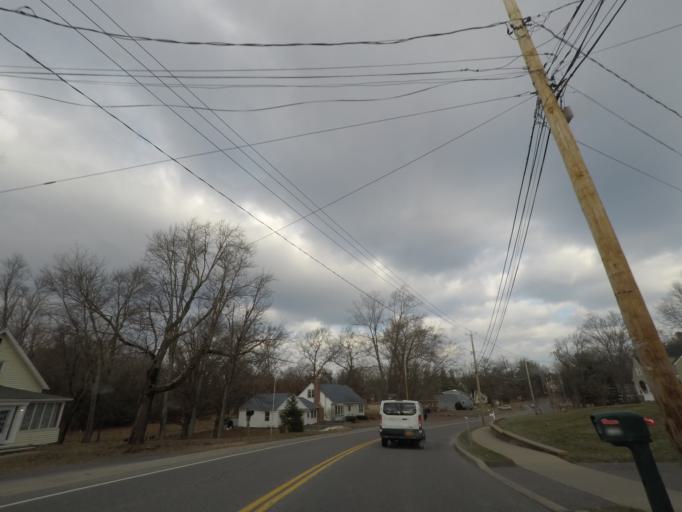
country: US
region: New York
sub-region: Albany County
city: Westmere
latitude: 42.6831
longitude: -73.8725
